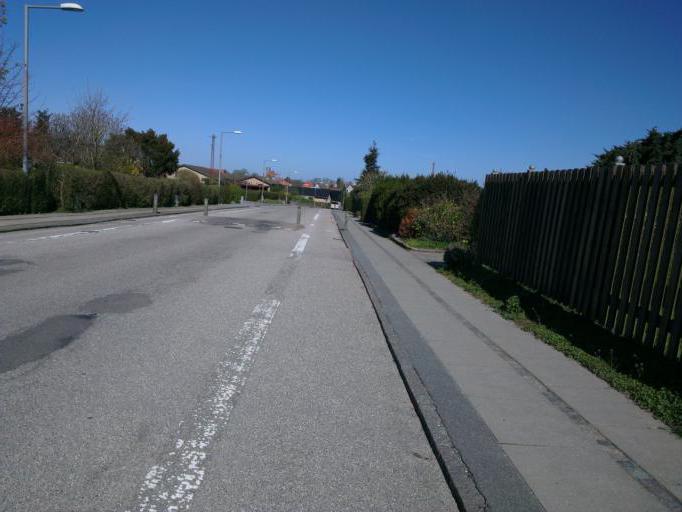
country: DK
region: Capital Region
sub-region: Frederikssund Kommune
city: Frederikssund
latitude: 55.8346
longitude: 12.0759
